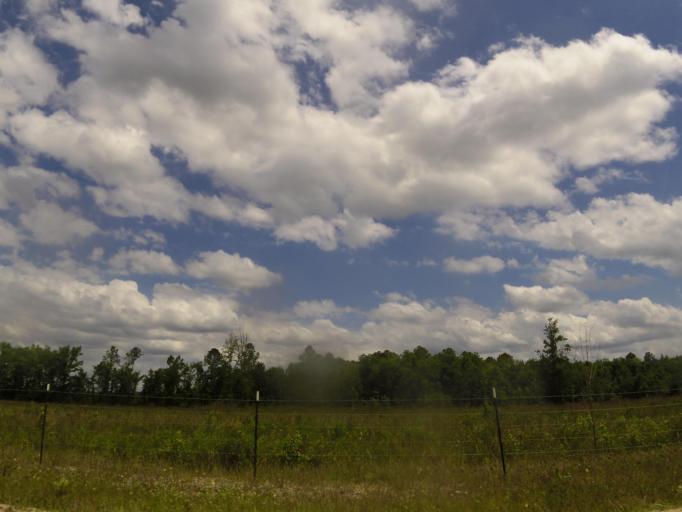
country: US
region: Florida
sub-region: Clay County
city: Asbury Lake
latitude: 29.8969
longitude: -81.8348
